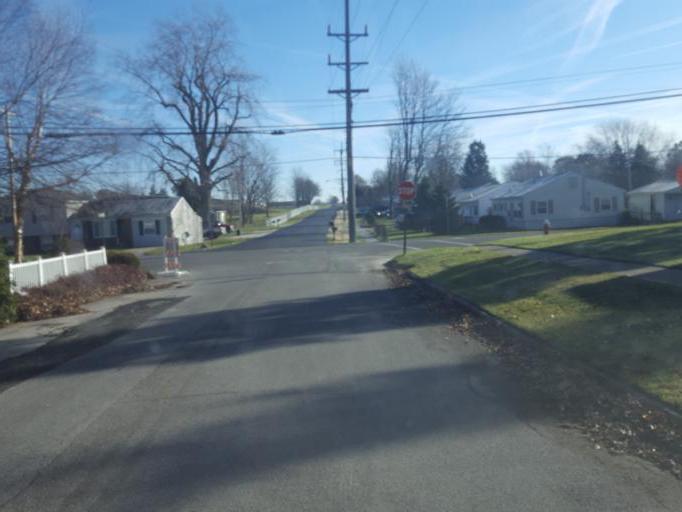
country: US
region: Ohio
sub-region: Crawford County
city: Bucyrus
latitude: 40.7978
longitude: -82.9594
